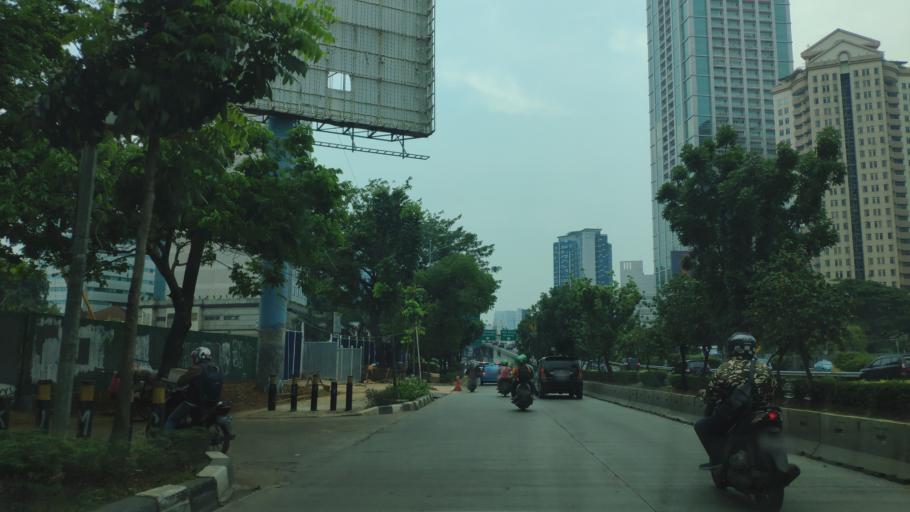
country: ID
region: Jakarta Raya
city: Jakarta
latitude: -6.1983
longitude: 106.7984
